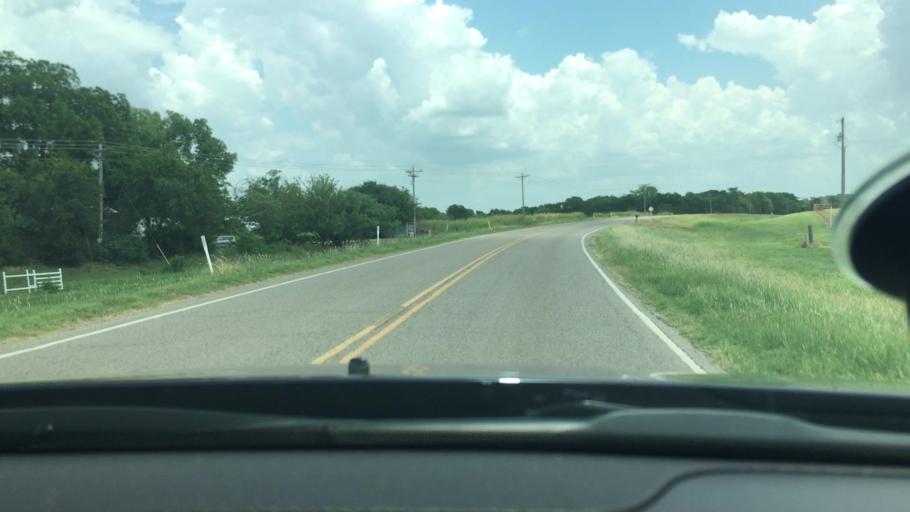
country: US
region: Oklahoma
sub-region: Love County
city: Marietta
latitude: 33.9400
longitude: -97.1006
